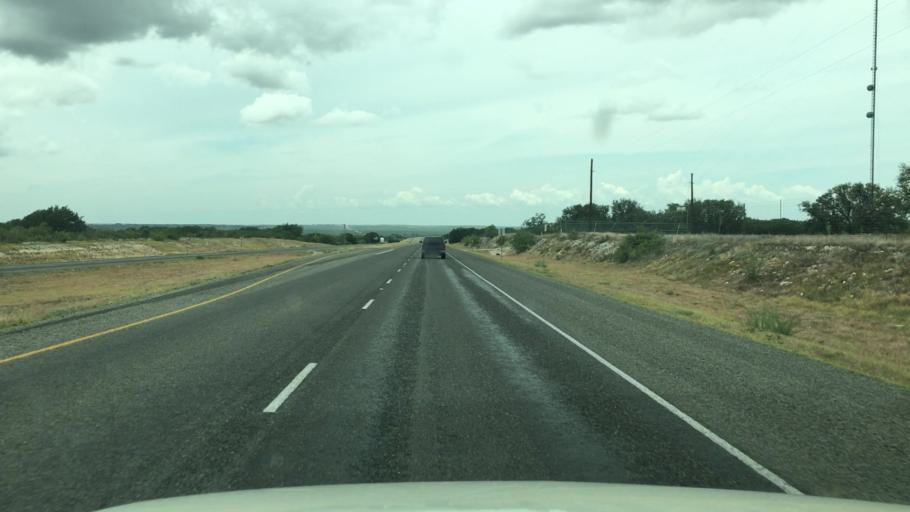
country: US
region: Texas
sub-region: Concho County
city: Eden
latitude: 31.2259
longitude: -99.9783
